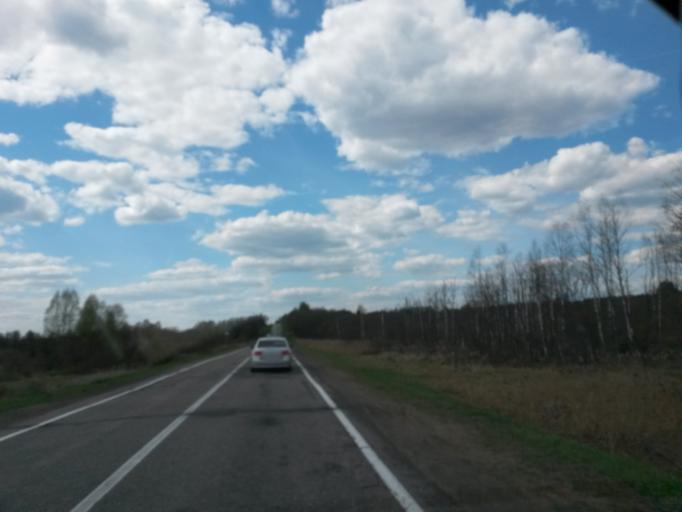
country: RU
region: Jaroslavl
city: Bol'shoye Selo
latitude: 57.7265
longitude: 39.0378
